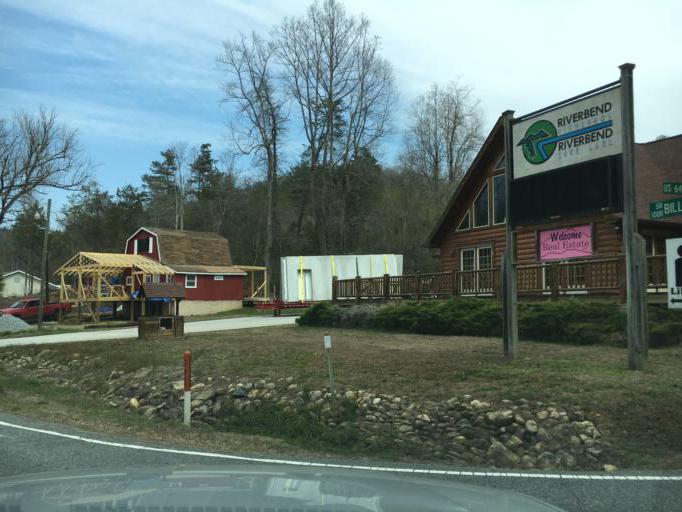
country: US
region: North Carolina
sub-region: Rutherford County
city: Lake Lure
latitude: 35.4244
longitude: -82.1624
